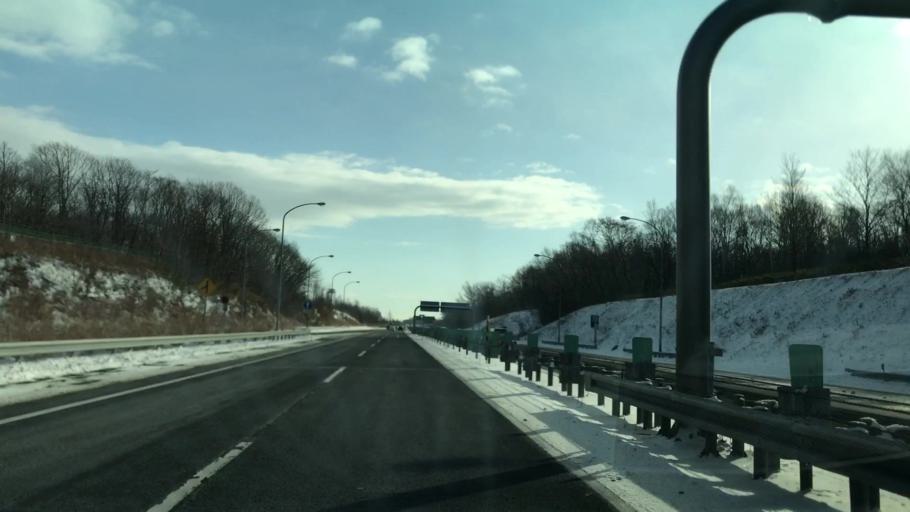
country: JP
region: Hokkaido
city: Chitose
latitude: 42.8442
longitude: 141.5885
